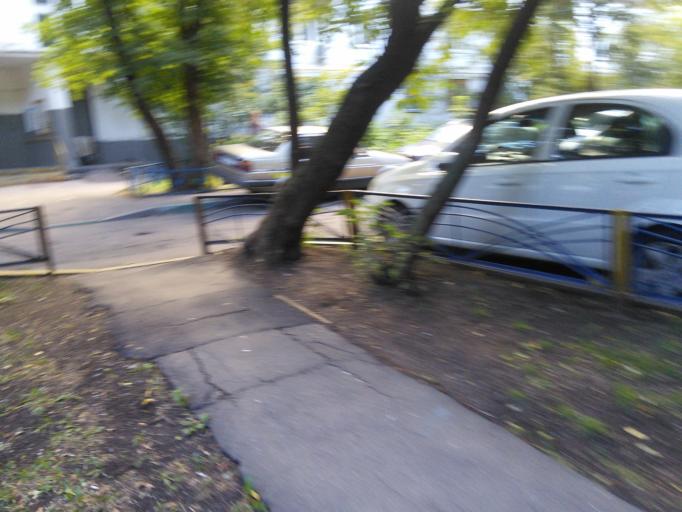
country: RU
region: Moskovskaya
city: Levoberezhnyy
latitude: 55.8467
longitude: 37.4449
